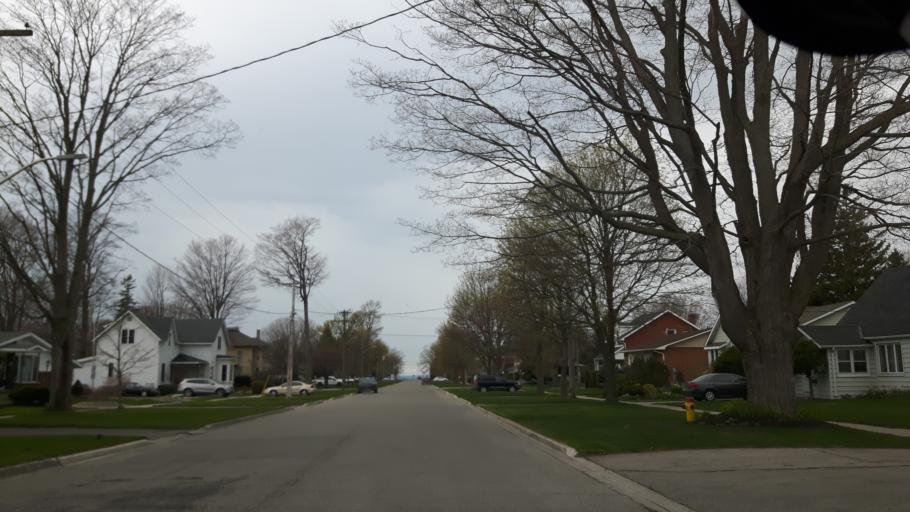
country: CA
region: Ontario
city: Goderich
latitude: 43.7406
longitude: -81.7197
